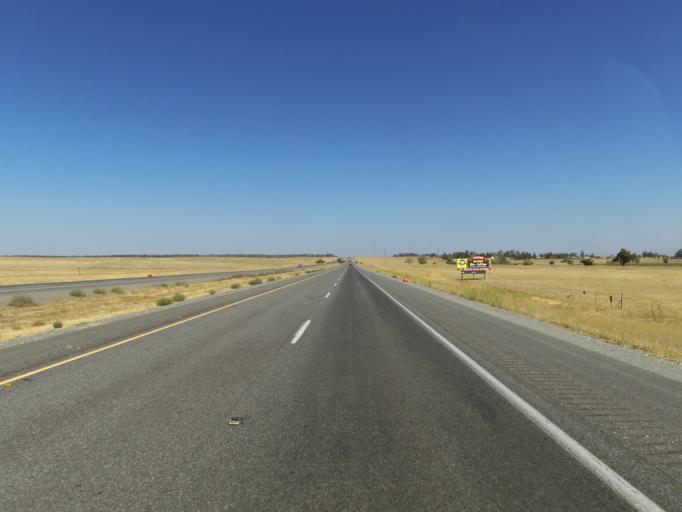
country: US
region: California
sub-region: Glenn County
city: Orland
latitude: 39.8234
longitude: -122.1998
